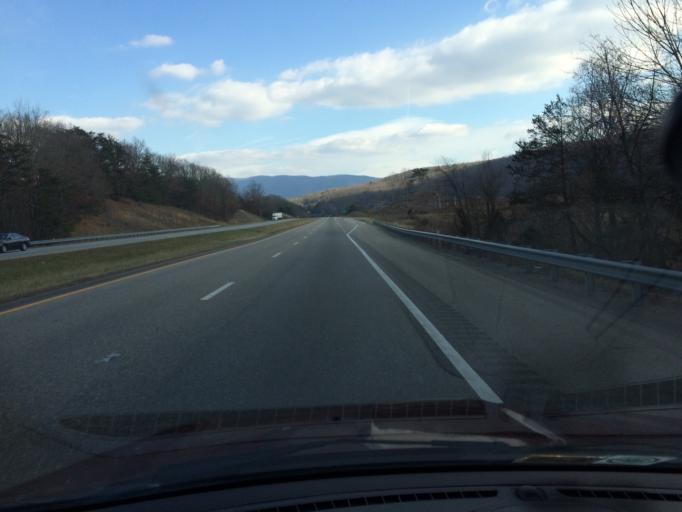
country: US
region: Virginia
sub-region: Alleghany County
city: Clifton Forge
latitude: 37.8278
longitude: -79.8024
